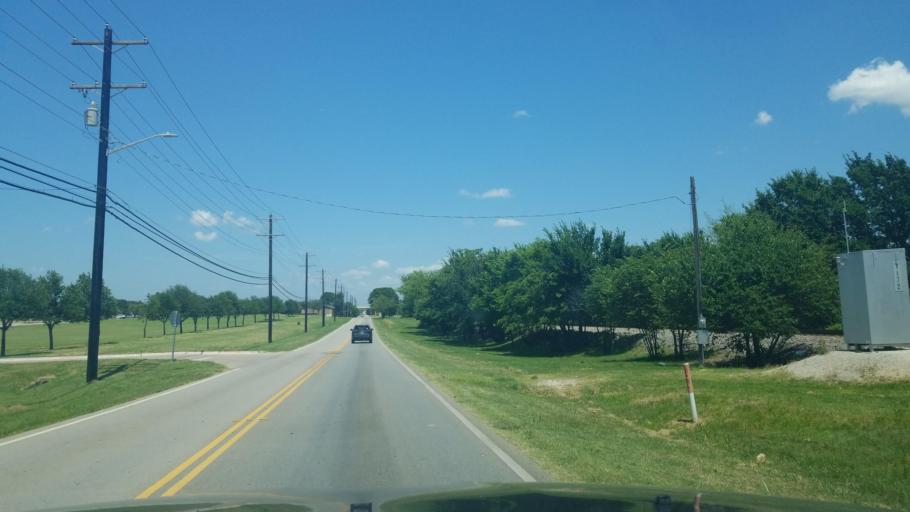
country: US
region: Texas
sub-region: Denton County
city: Denton
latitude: 33.2316
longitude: -97.1050
